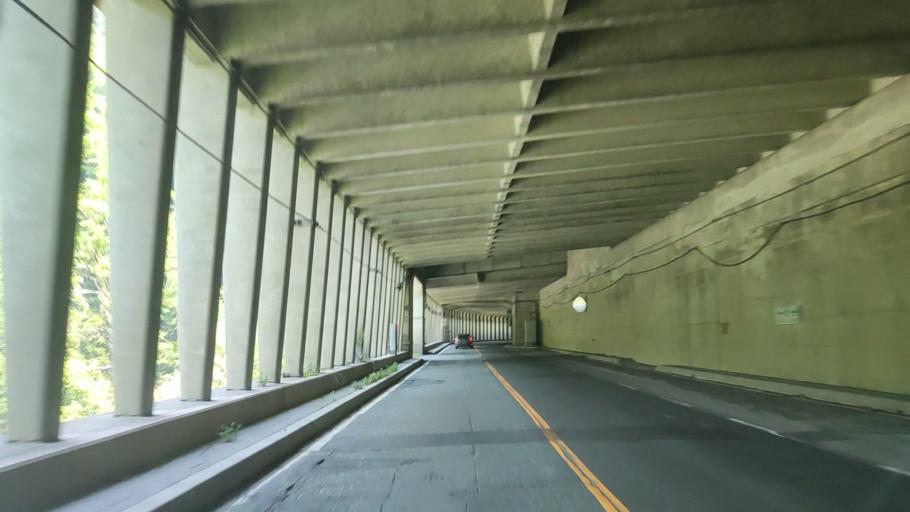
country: JP
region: Niigata
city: Itoigawa
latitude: 36.9115
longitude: 137.8630
